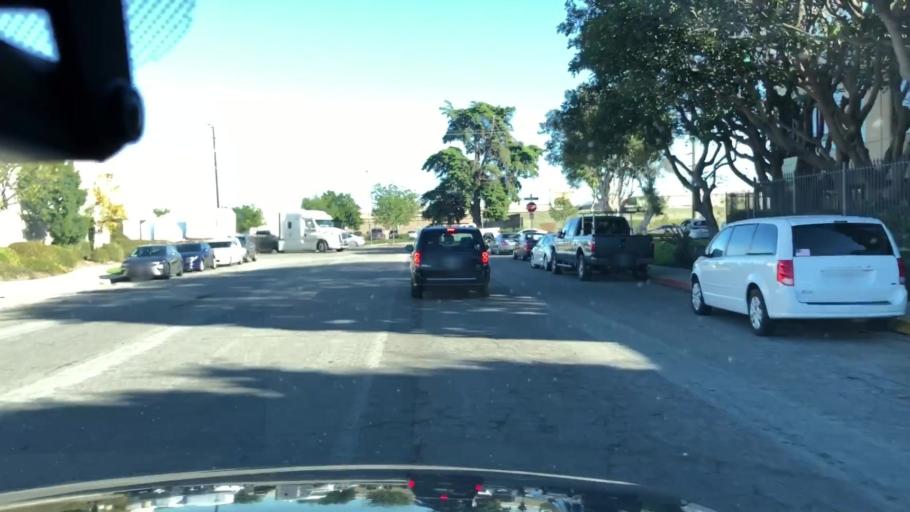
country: US
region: California
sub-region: Ventura County
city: El Rio
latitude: 34.2202
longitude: -119.1547
